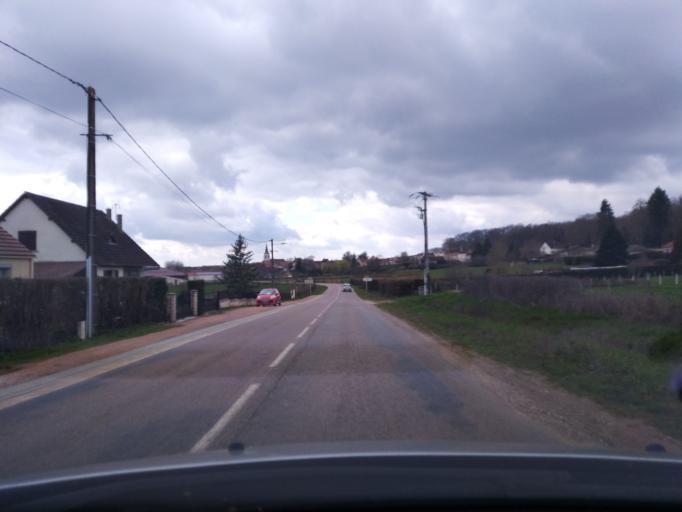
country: FR
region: Bourgogne
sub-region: Departement de l'Yonne
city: Avallon
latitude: 47.5172
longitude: 3.9459
